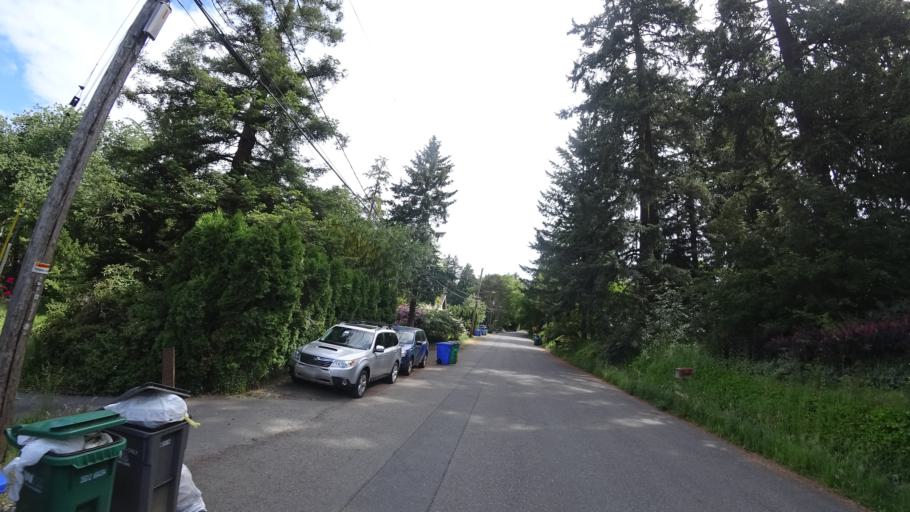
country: US
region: Oregon
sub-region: Clackamas County
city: Lake Oswego
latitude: 45.4582
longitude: -122.6886
